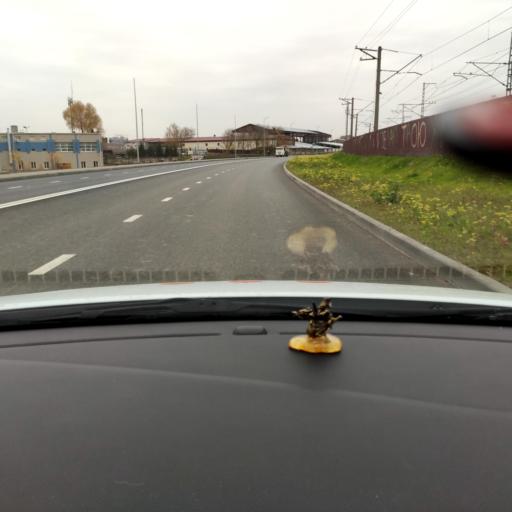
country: RU
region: Tatarstan
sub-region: Gorod Kazan'
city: Kazan
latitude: 55.8069
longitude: 49.0546
